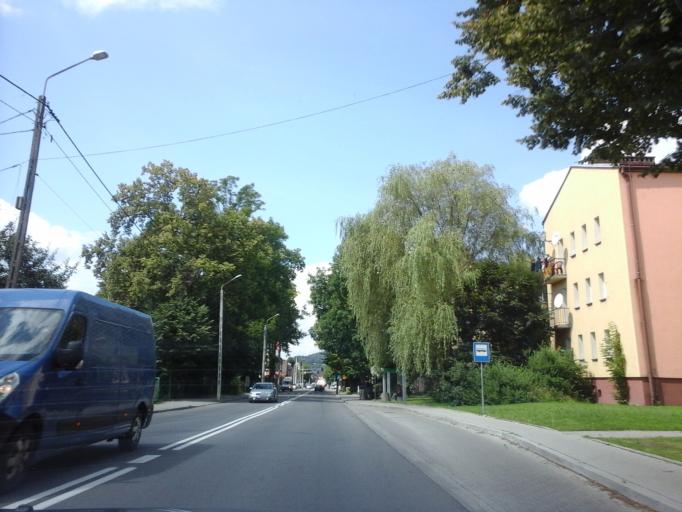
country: PL
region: Lesser Poland Voivodeship
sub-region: Powiat suski
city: Makow Podhalanski
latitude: 49.7280
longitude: 19.6826
